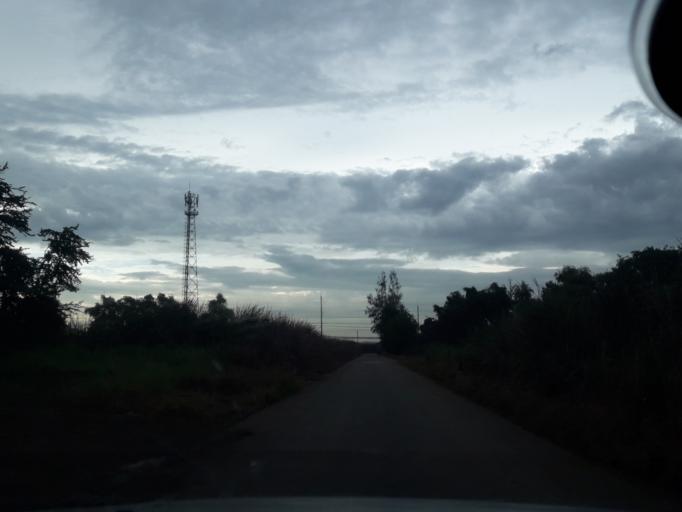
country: TH
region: Phra Nakhon Si Ayutthaya
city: Wang Noi
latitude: 14.2607
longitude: 100.7821
